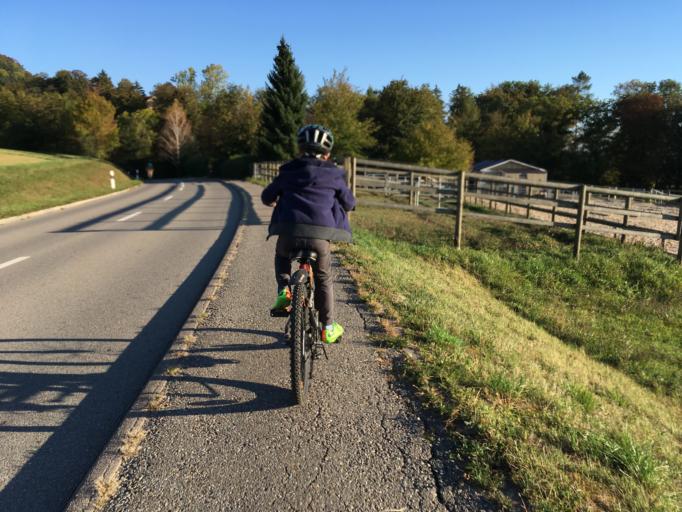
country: CH
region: Zurich
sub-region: Bezirk Buelach
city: Rorbas
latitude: 47.5460
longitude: 8.5691
